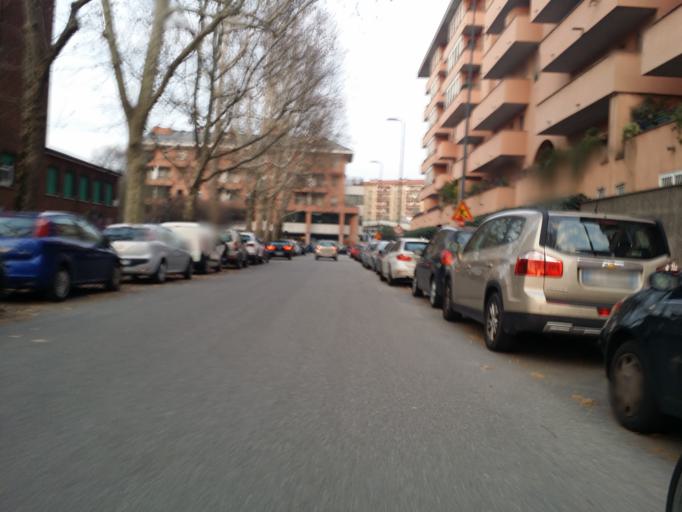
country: IT
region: Lombardy
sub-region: Citta metropolitana di Milano
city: Romano Banco
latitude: 45.4543
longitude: 9.1209
